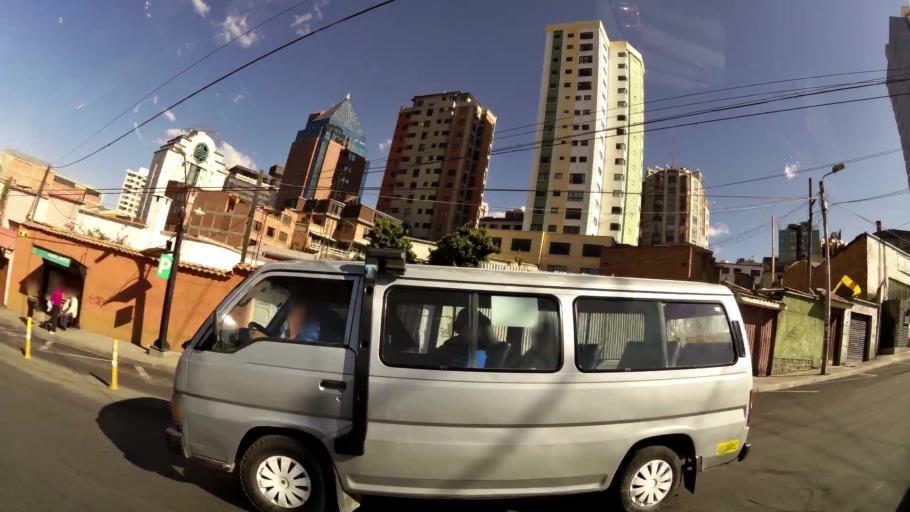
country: BO
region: La Paz
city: La Paz
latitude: -16.5045
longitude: -68.1277
